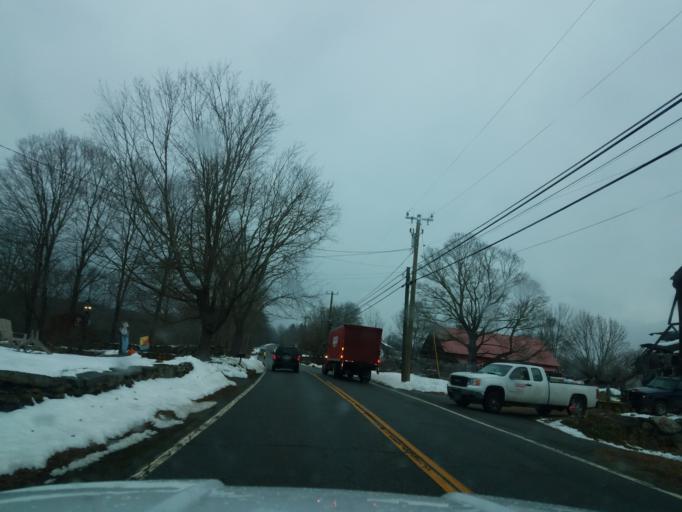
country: US
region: Connecticut
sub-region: Windham County
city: South Woodstock
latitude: 41.9652
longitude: -71.9858
